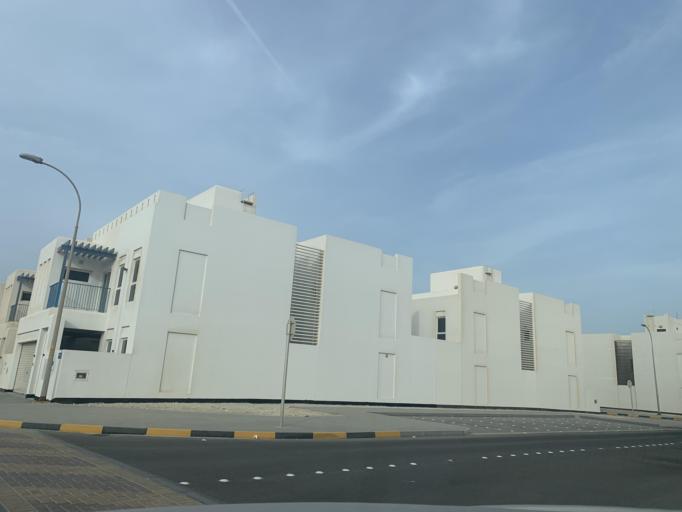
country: BH
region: Muharraq
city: Al Muharraq
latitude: 26.3160
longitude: 50.6208
